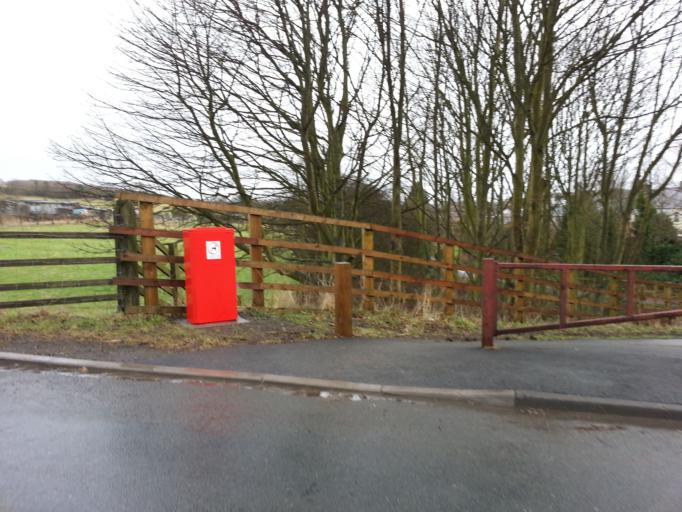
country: GB
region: England
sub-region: County Durham
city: Crook
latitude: 54.7596
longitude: -1.7278
